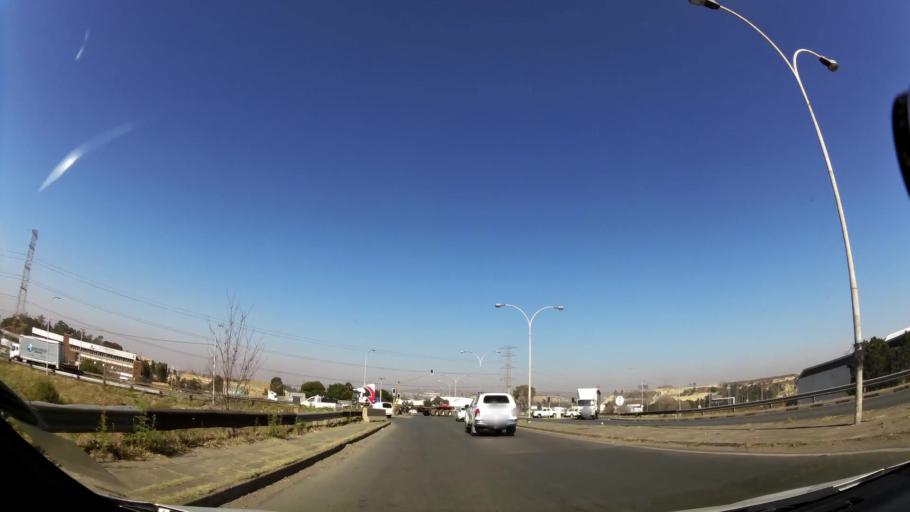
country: ZA
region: Gauteng
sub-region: Ekurhuleni Metropolitan Municipality
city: Germiston
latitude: -26.2095
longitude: 28.1170
